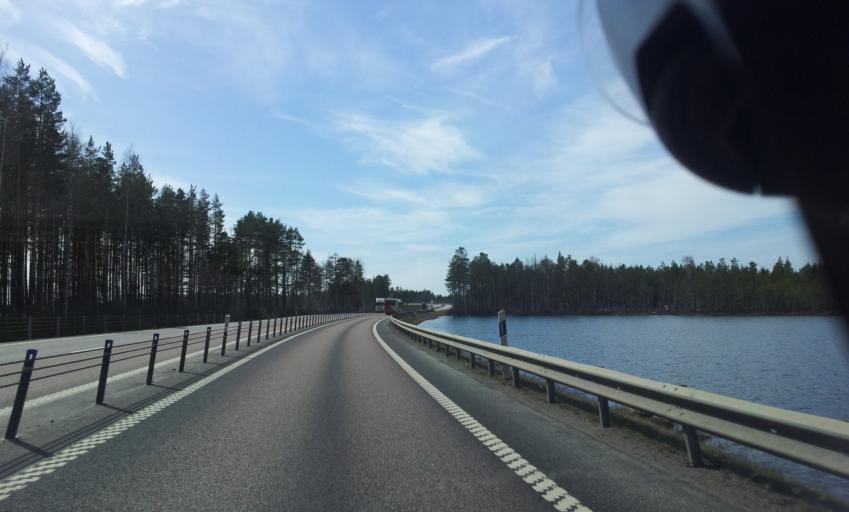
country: SE
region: Gaevleborg
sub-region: Gavle Kommun
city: Norrsundet
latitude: 61.0812
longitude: 16.9718
